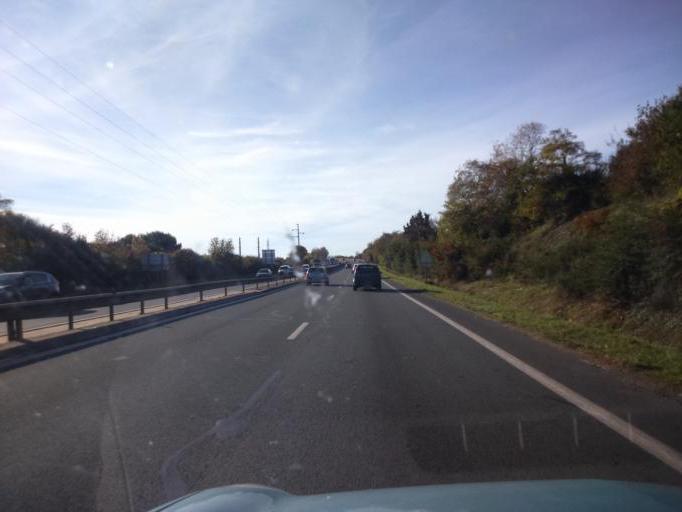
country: FR
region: Poitou-Charentes
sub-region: Departement de la Charente-Maritime
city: Puilboreau
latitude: 46.1672
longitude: -1.1213
